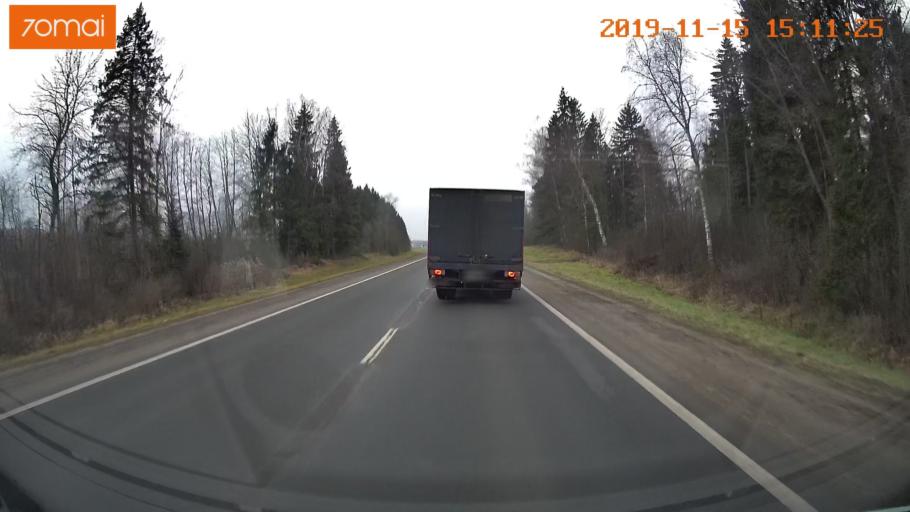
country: RU
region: Jaroslavl
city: Prechistoye
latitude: 58.3367
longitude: 40.2412
